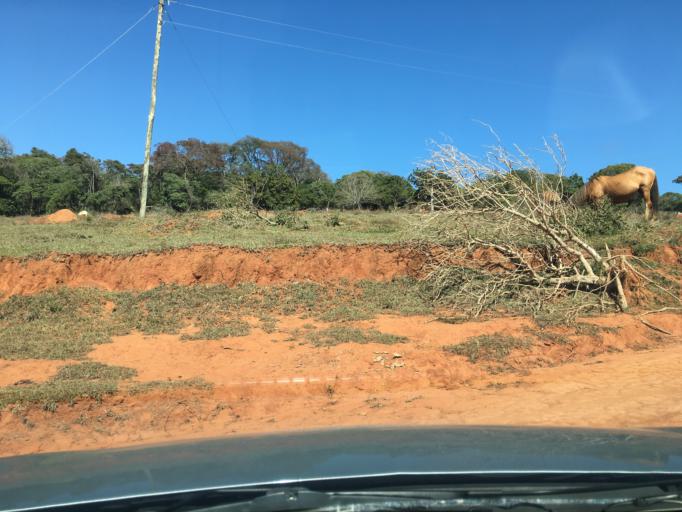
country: BR
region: Minas Gerais
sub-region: Campestre
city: Campestre
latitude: -21.5972
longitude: -46.2055
